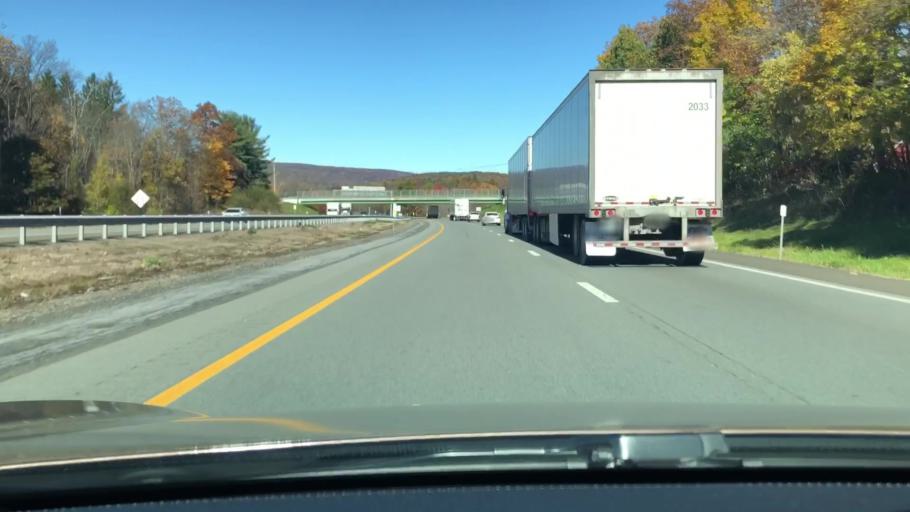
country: US
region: New York
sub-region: Orange County
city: Central Valley
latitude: 41.3241
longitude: -74.1125
